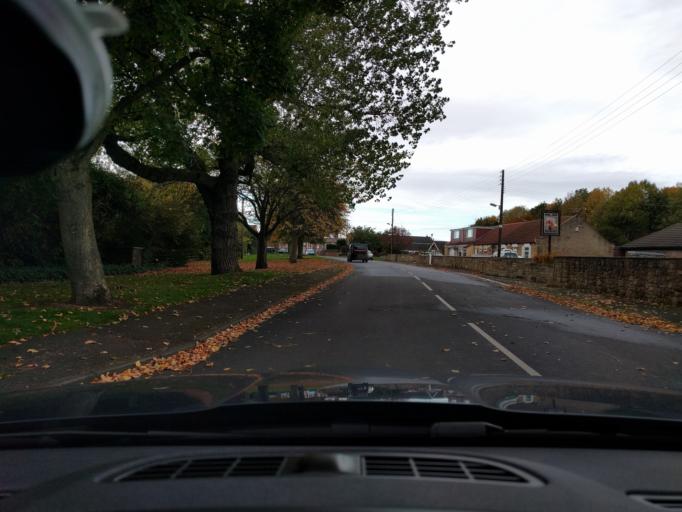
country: GB
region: England
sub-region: Northumberland
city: Blyth
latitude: 55.1444
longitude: -1.5471
